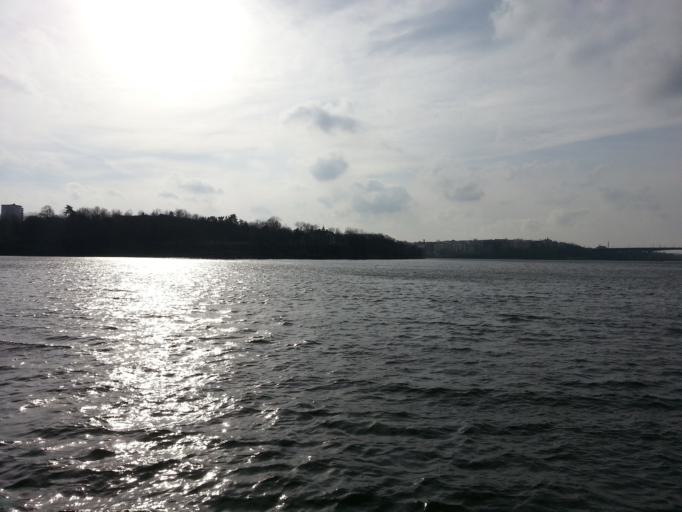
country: SE
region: Stockholm
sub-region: Solna Kommun
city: Solna
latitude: 59.3251
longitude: 18.0209
